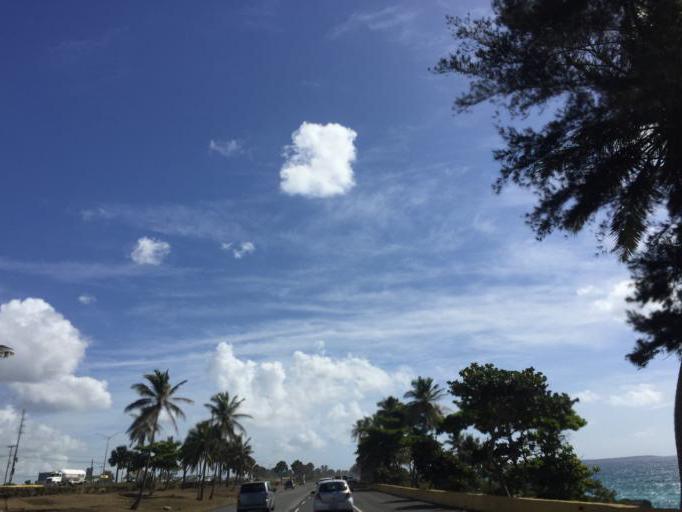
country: DO
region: Santo Domingo
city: Guerra
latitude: 18.4596
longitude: -69.7269
